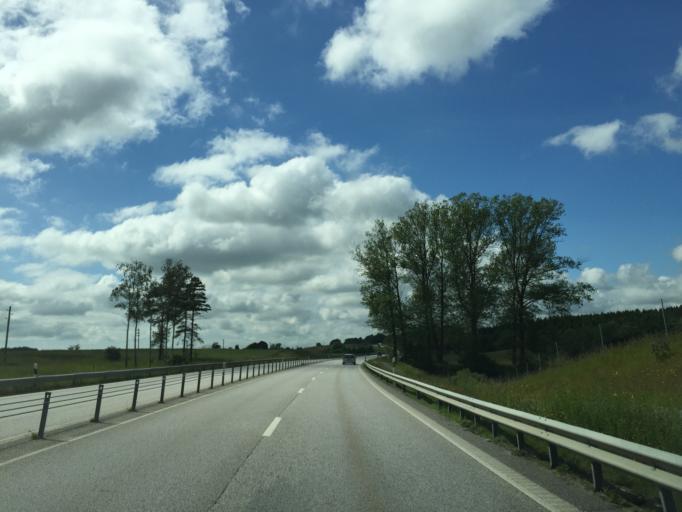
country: SE
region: Skane
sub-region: Skurups Kommun
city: Skurup
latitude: 55.4978
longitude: 13.4188
